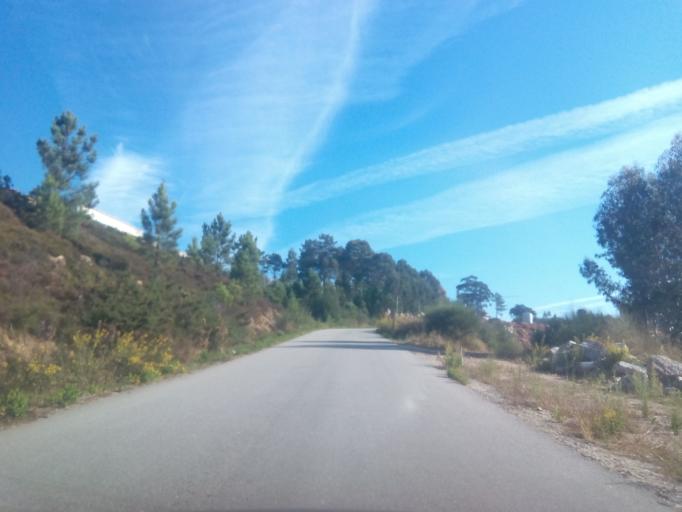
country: PT
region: Porto
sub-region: Paredes
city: Gandra
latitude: 41.2033
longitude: -8.4327
